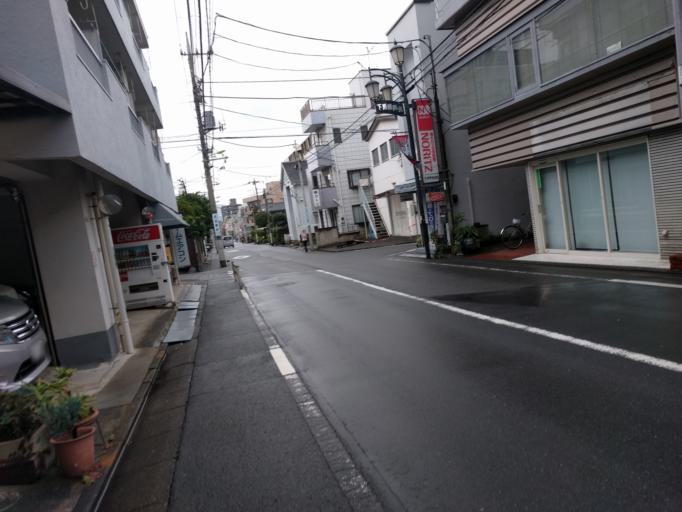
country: JP
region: Tokyo
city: Tokyo
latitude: 35.6355
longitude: 139.6804
